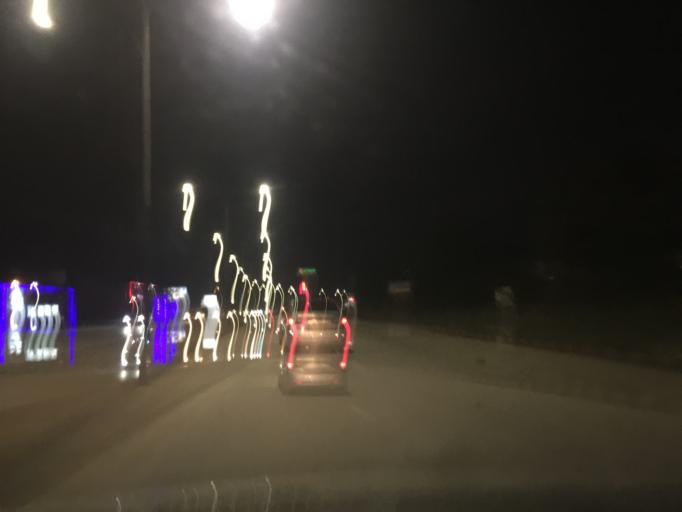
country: JO
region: Amman
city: Umm as Summaq
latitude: 31.8811
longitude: 35.8430
